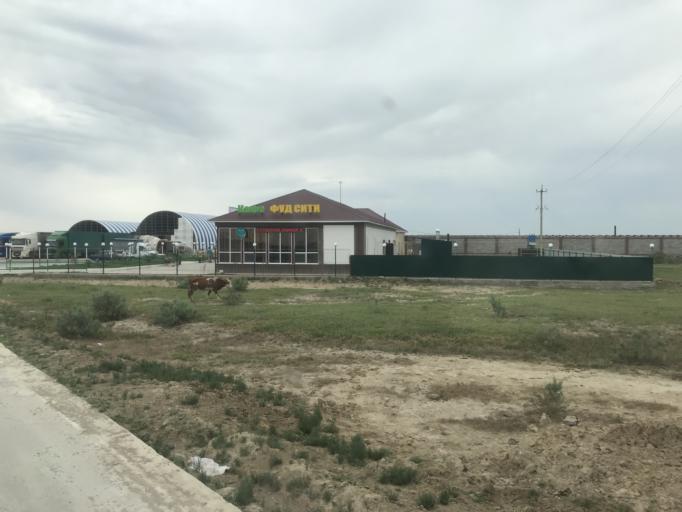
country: KZ
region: Ongtustik Qazaqstan
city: Asykata
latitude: 40.9617
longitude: 68.4608
